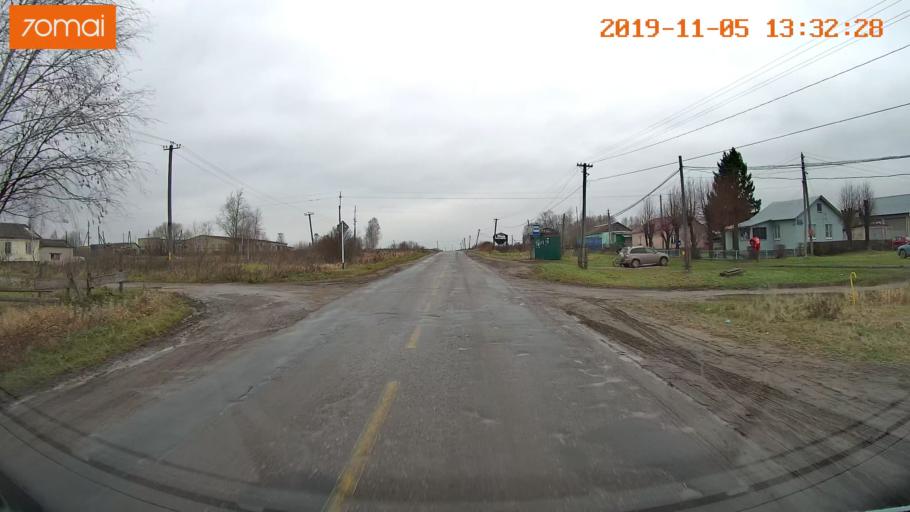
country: RU
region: Ivanovo
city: Shuya
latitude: 56.8833
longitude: 41.3978
